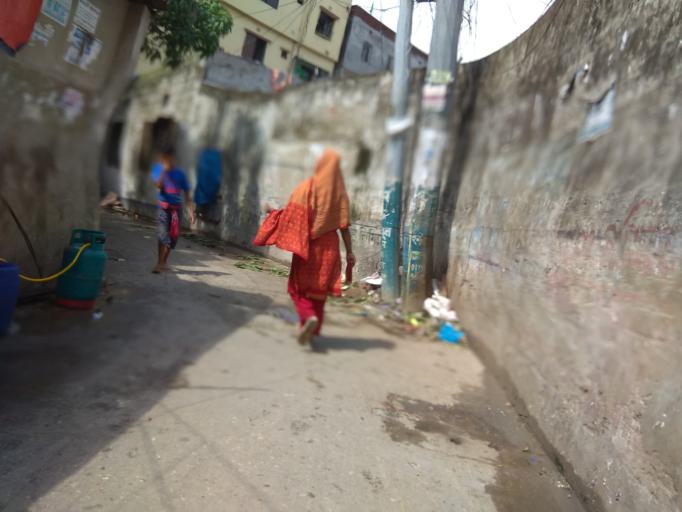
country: BD
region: Dhaka
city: Azimpur
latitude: 23.7977
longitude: 90.3568
